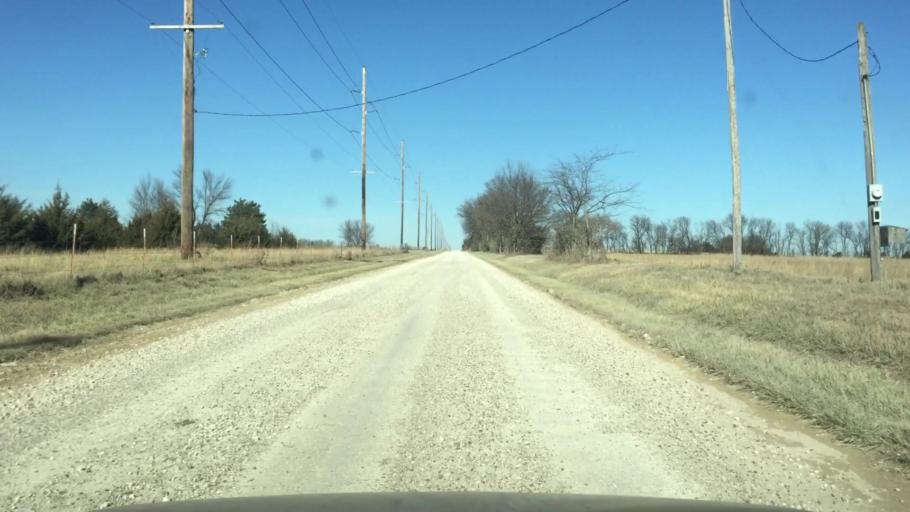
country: US
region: Kansas
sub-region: Allen County
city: Humboldt
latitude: 37.8280
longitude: -95.4185
